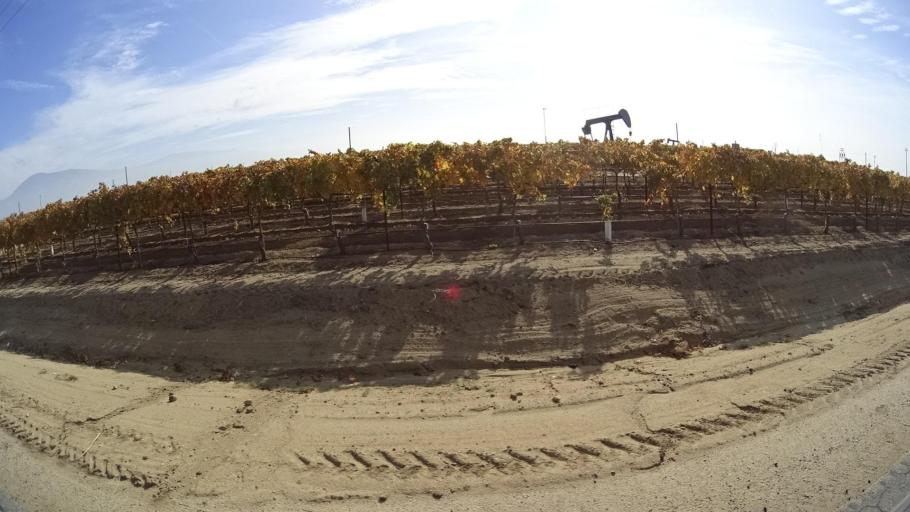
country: US
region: California
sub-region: Kern County
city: Lamont
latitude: 35.3110
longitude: -118.8280
